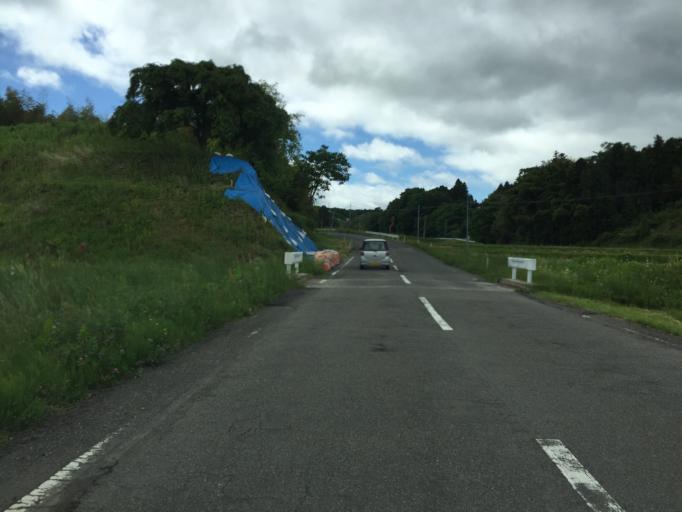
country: JP
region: Fukushima
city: Miharu
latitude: 37.4815
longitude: 140.4682
